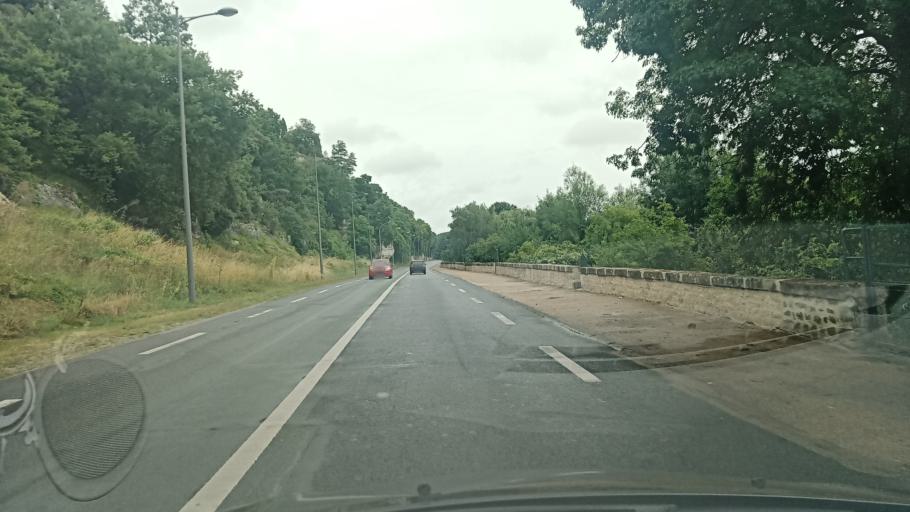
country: FR
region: Poitou-Charentes
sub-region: Departement de la Vienne
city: Poitiers
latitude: 46.5997
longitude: 0.3390
